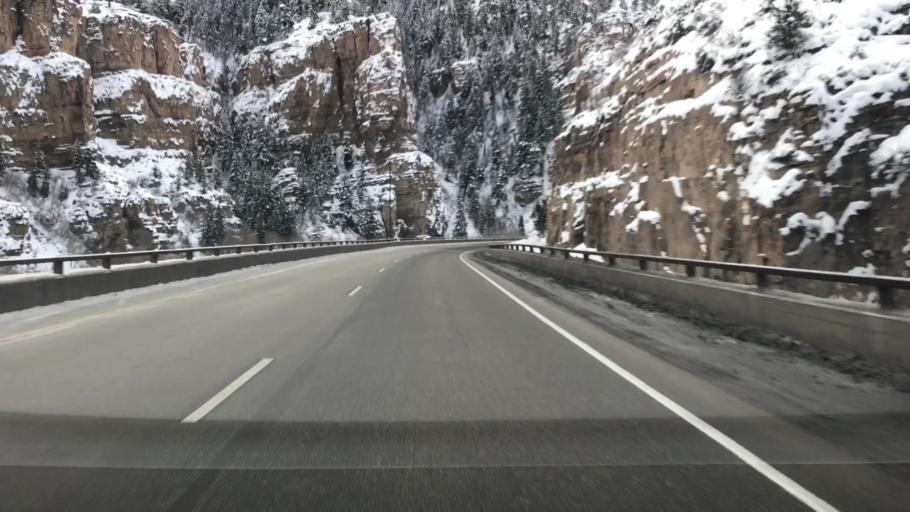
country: US
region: Colorado
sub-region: Garfield County
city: Glenwood Springs
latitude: 39.6063
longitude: -107.1560
